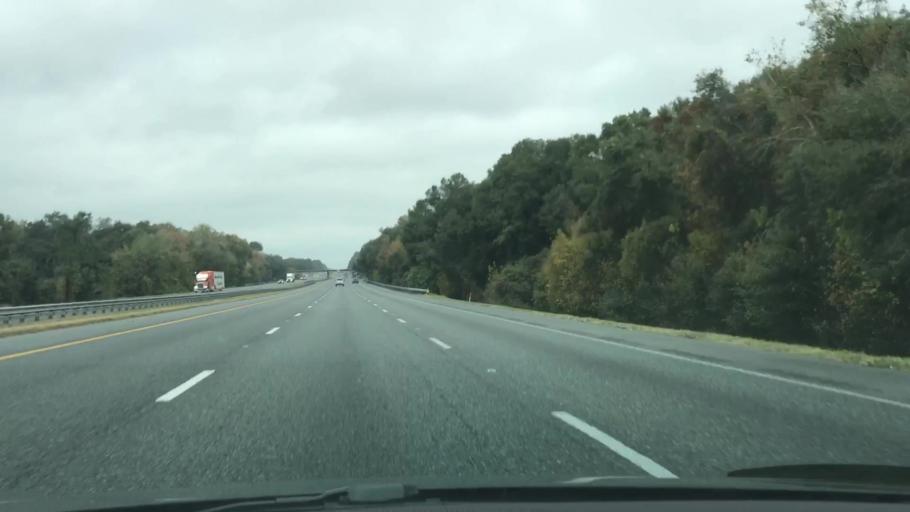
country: US
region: Florida
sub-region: Columbia County
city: Lake City
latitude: 30.0845
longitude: -82.6396
